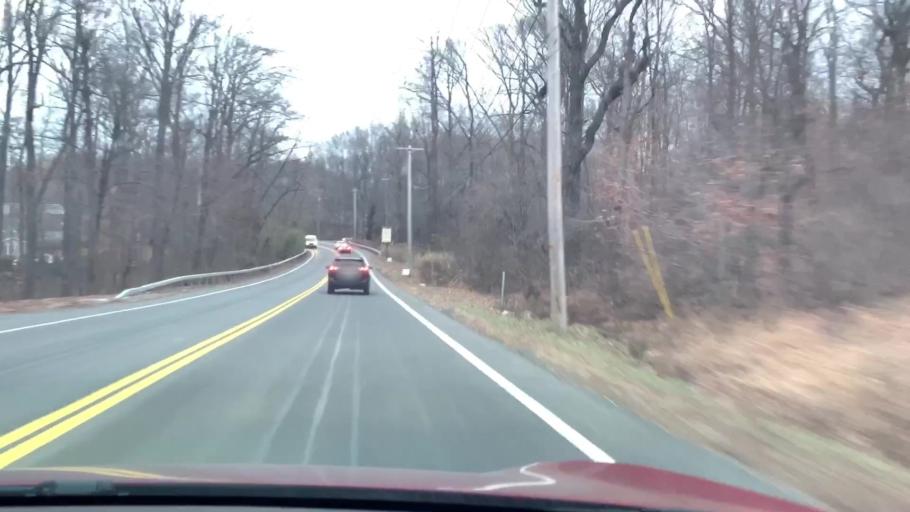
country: US
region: New York
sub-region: Rockland County
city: Sparkill
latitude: 41.0071
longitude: -73.9149
